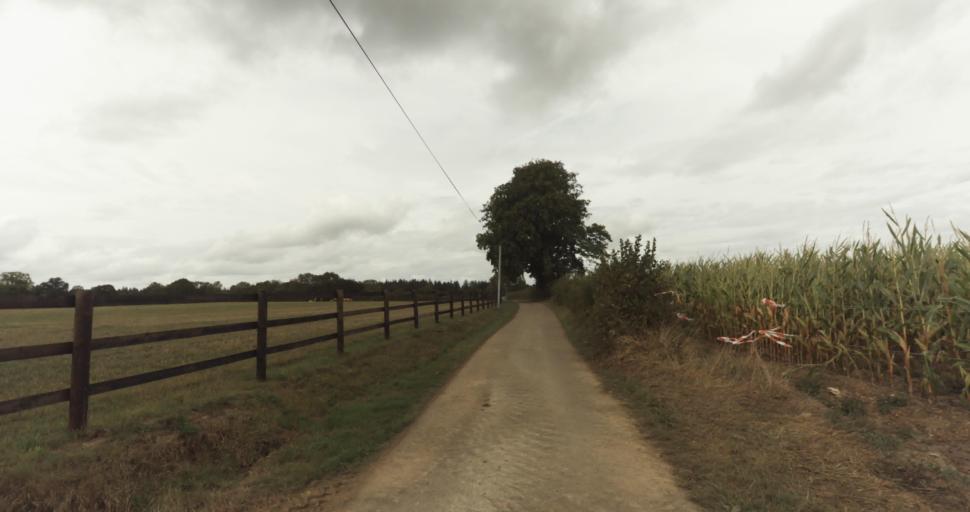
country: FR
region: Lower Normandy
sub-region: Departement de l'Orne
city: Gace
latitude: 48.8249
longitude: 0.3627
